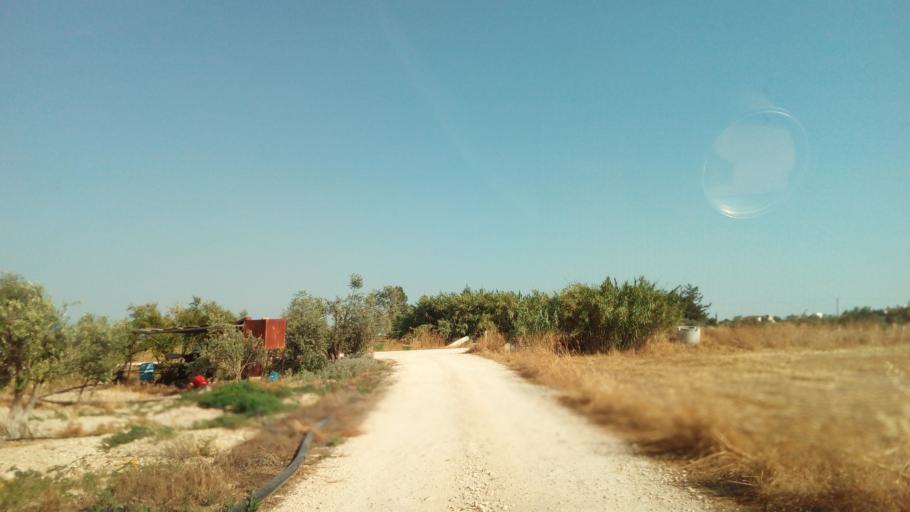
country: CY
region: Larnaka
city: Aradippou
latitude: 34.9608
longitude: 33.5988
